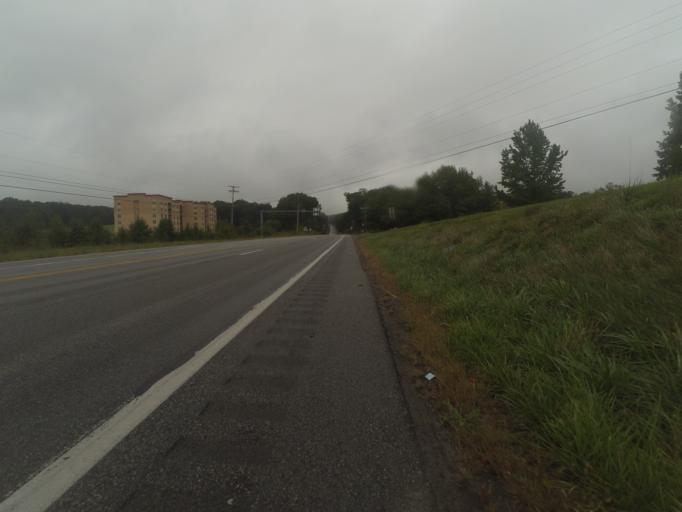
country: US
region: Pennsylvania
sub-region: Huntingdon County
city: Huntingdon
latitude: 40.4941
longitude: -78.0442
